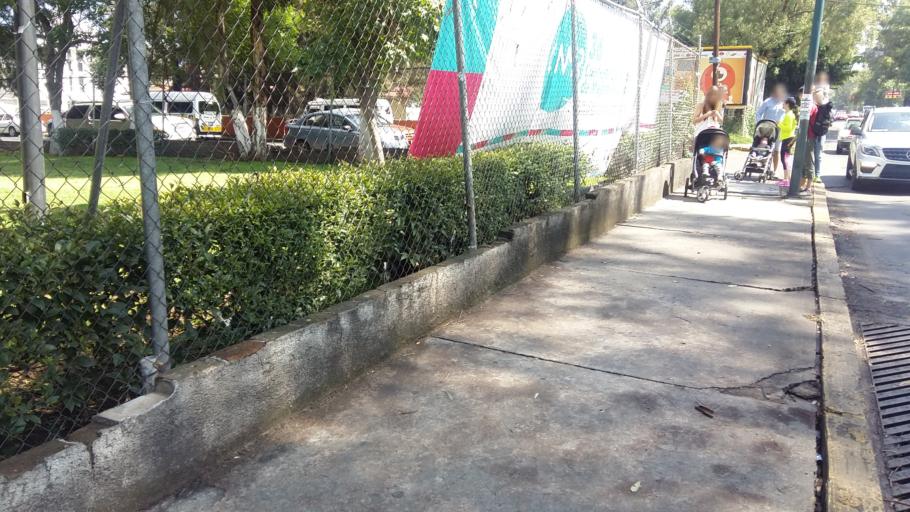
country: MX
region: Michoacan
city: Morelia
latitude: 19.6860
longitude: -101.1806
